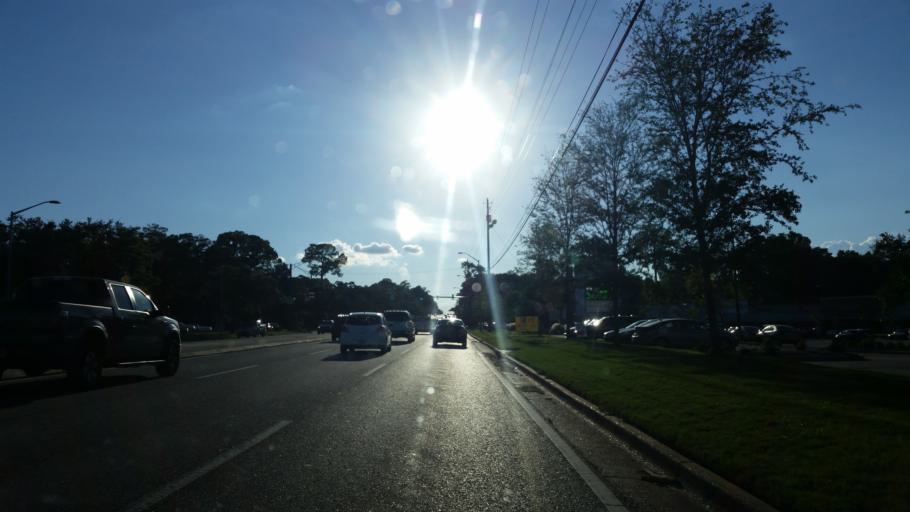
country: US
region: Alabama
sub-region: Mobile County
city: Tillmans Corner
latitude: 30.6762
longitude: -88.1504
